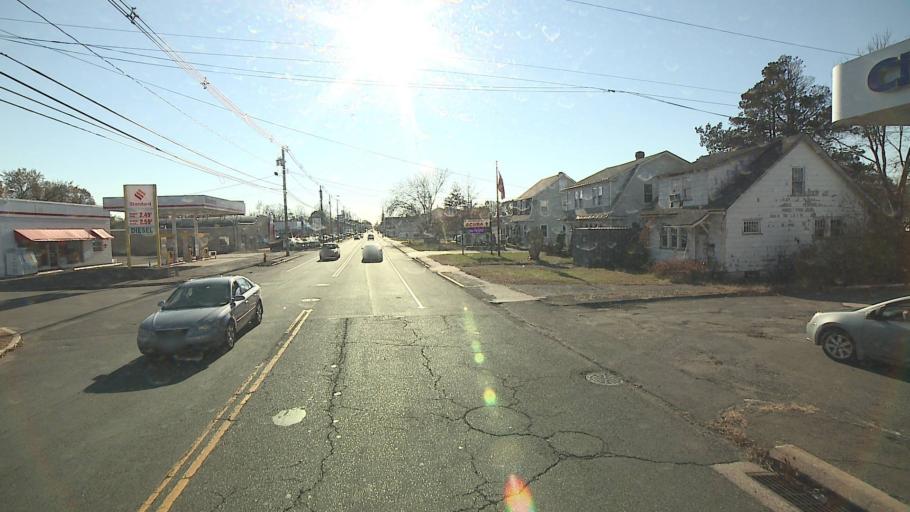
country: US
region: Connecticut
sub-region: New Haven County
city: Wallingford
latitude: 41.4665
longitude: -72.8185
